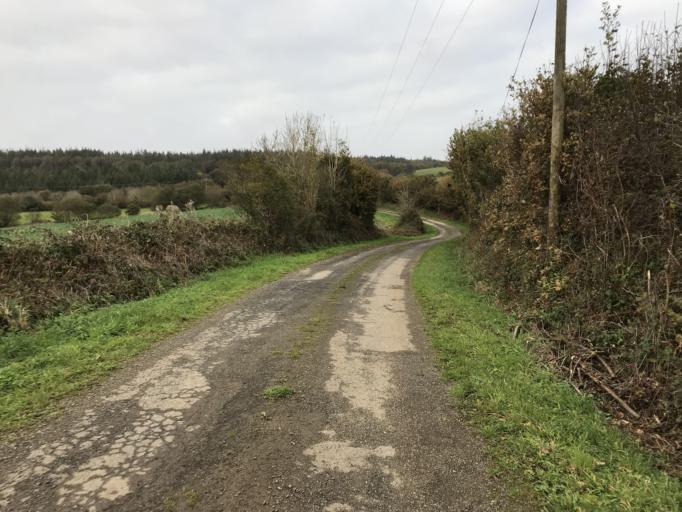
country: FR
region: Brittany
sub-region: Departement du Finistere
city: Hopital-Camfrout
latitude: 48.3231
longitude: -4.2144
